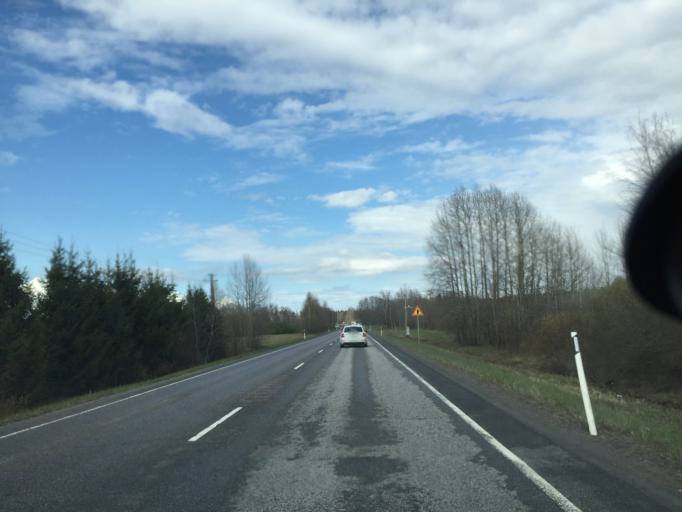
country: FI
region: Uusimaa
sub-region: Helsinki
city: Lohja
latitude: 60.2029
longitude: 24.0183
